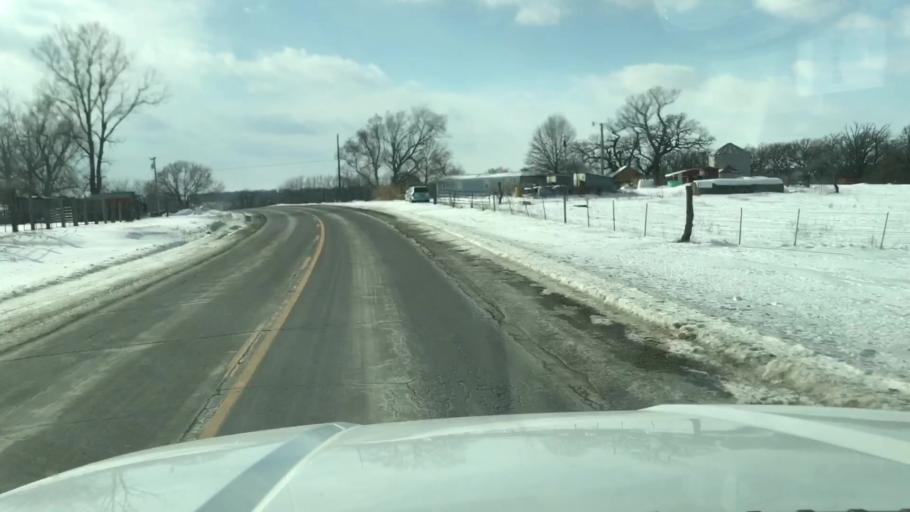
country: US
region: Missouri
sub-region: Gentry County
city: Stanberry
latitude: 40.3591
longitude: -94.6693
